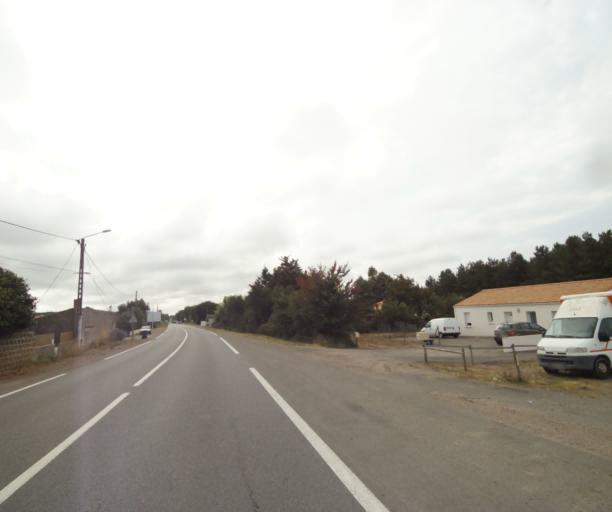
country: FR
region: Pays de la Loire
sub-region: Departement de la Vendee
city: Chateau-d'Olonne
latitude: 46.4814
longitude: -1.7149
